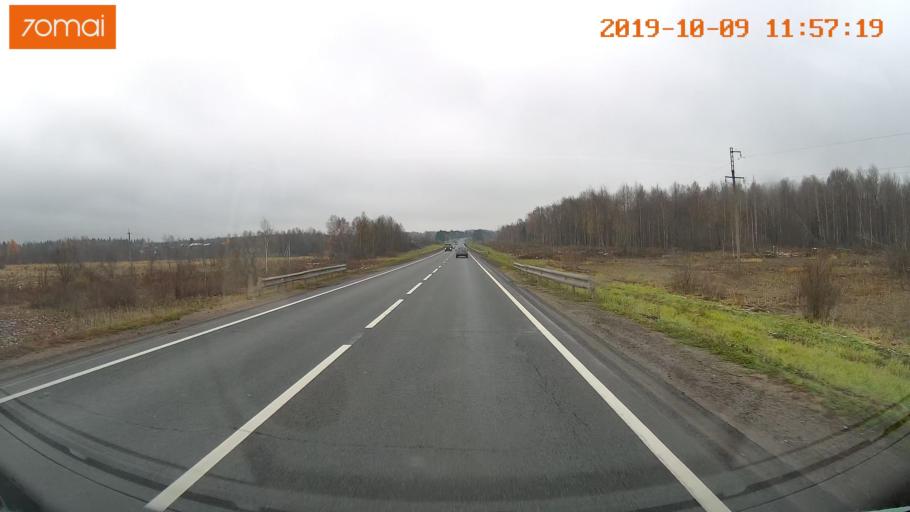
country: RU
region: Vologda
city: Gryazovets
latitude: 58.7338
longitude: 40.2919
